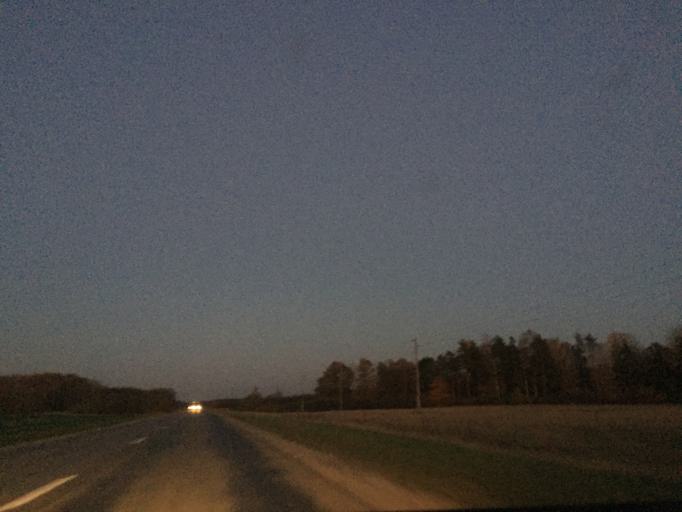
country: LV
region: Tervete
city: Zelmeni
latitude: 56.5102
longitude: 23.2952
